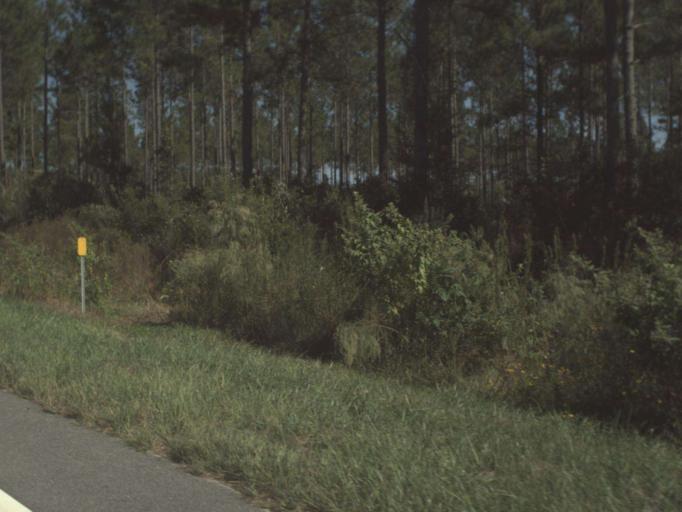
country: US
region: Florida
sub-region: Jefferson County
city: Monticello
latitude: 30.4426
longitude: -84.0190
